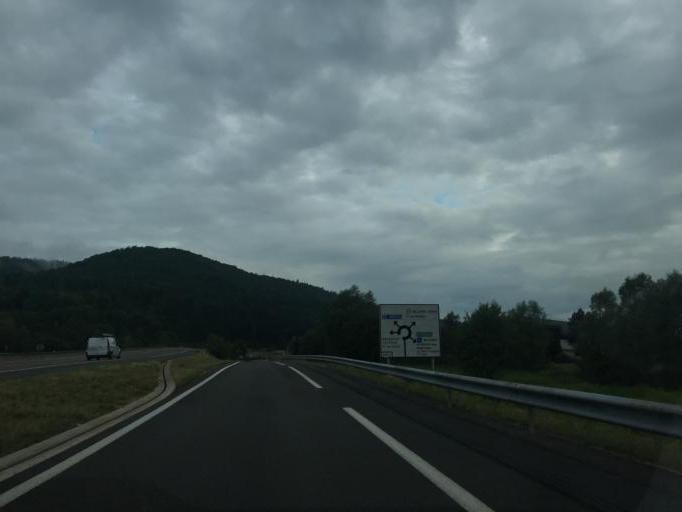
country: FR
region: Rhone-Alpes
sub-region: Departement de l'Ain
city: Bellignat
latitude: 46.2313
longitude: 5.6195
